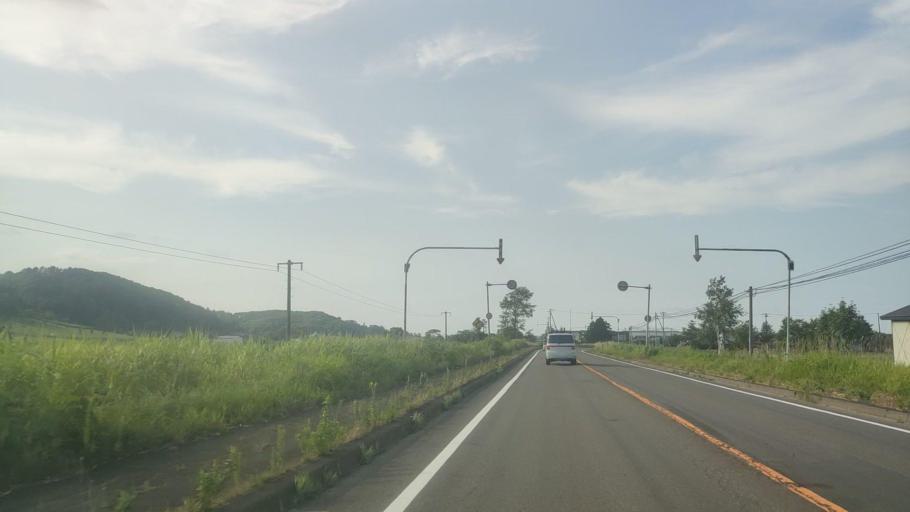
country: JP
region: Hokkaido
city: Iwamizawa
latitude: 43.0012
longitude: 141.7888
